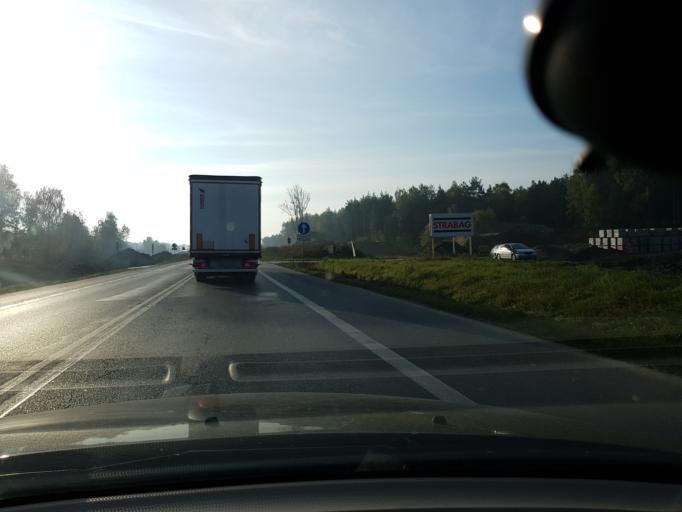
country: PL
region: Masovian Voivodeship
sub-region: Powiat otwocki
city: Otwock
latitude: 52.1628
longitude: 21.3011
